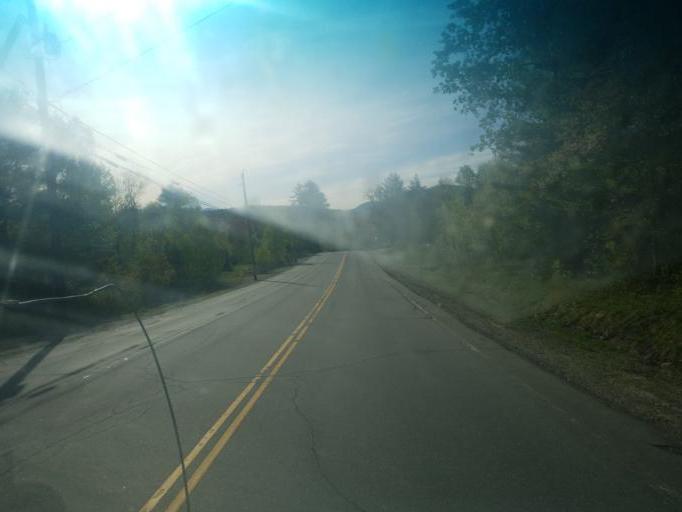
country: US
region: New Hampshire
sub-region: Grafton County
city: Deerfield
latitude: 44.2782
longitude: -71.6450
